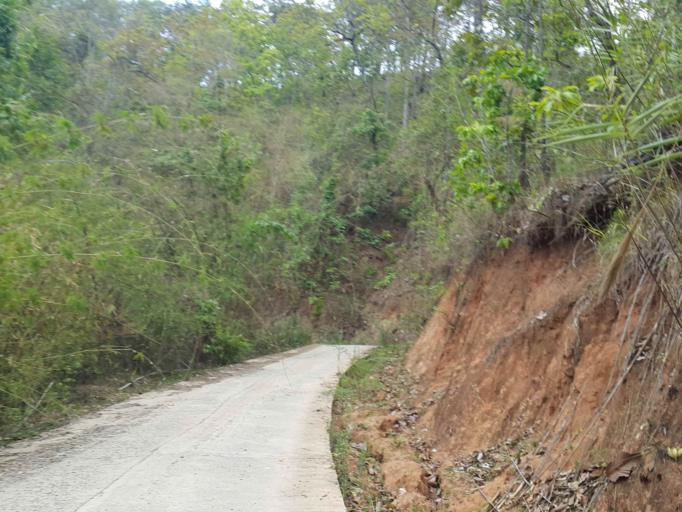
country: TH
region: Chiang Mai
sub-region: Amphoe Chiang Dao
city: Chiang Dao
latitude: 19.2935
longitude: 98.7552
